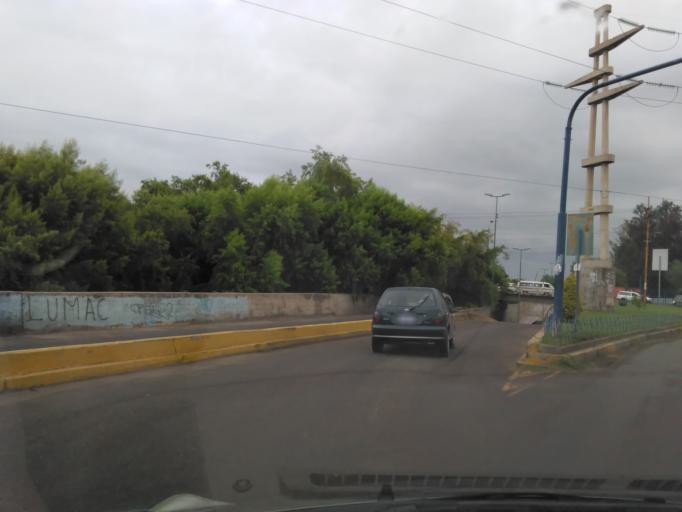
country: BO
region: Cochabamba
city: Cochabamba
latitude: -17.3961
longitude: -66.1679
